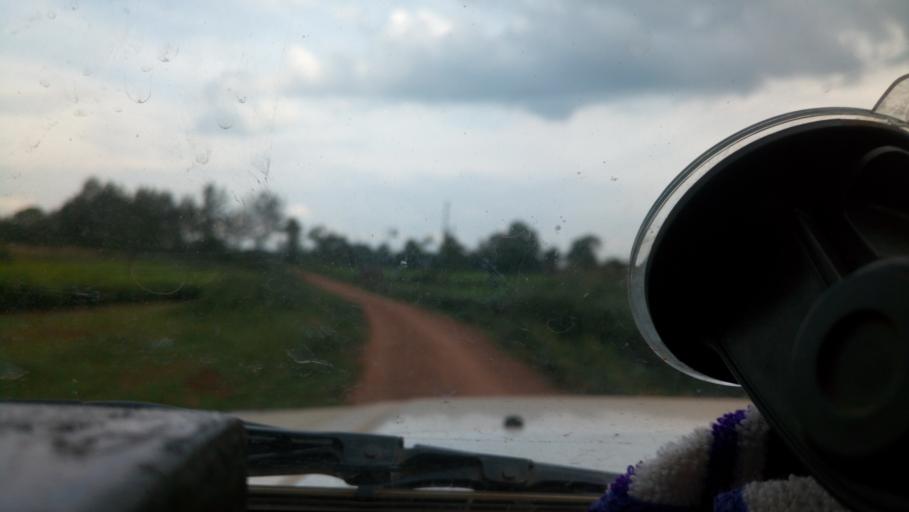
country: KE
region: Kericho
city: Litein
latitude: -0.5889
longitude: 35.1303
